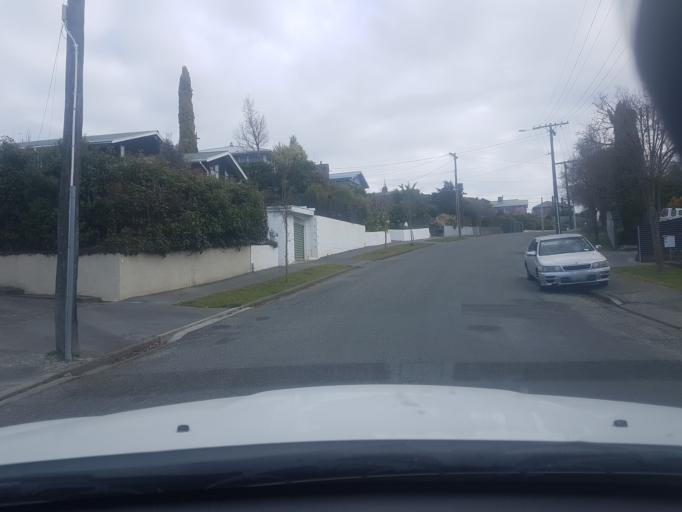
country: NZ
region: Canterbury
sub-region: Timaru District
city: Timaru
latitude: -44.3924
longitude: 171.2176
